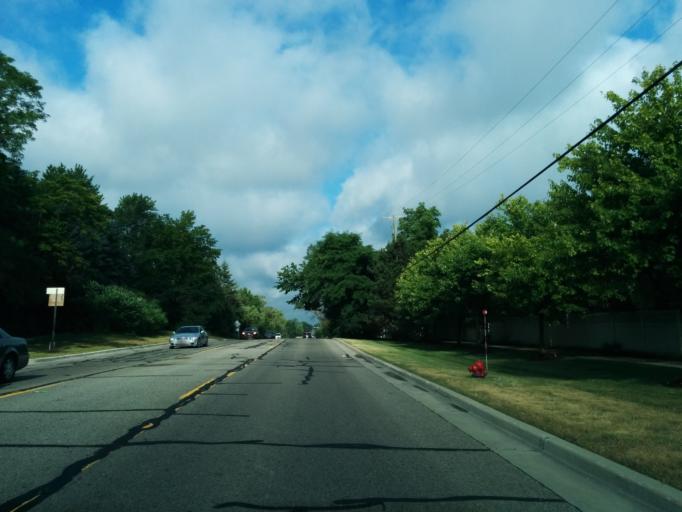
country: US
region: Michigan
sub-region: Oakland County
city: West Bloomfield Township
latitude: 42.5278
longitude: -83.3836
